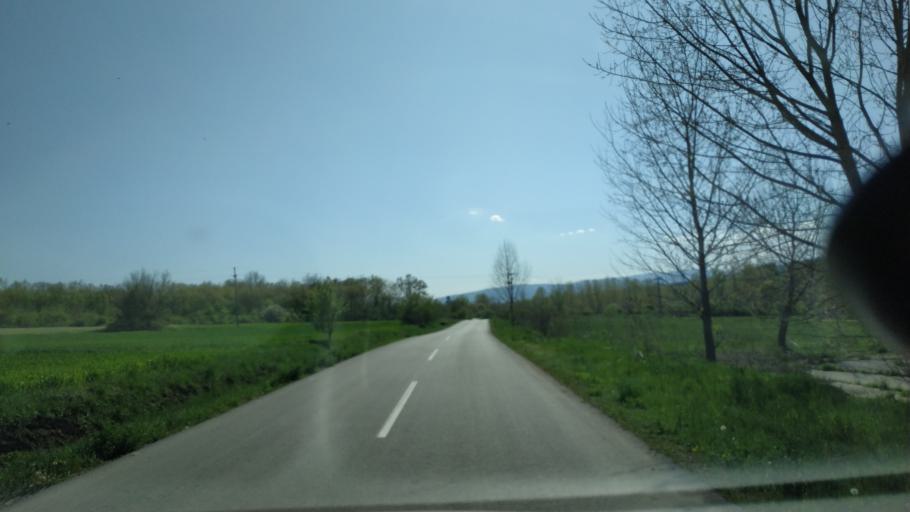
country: RS
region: Central Serbia
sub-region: Nisavski Okrug
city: Nis
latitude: 43.4603
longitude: 21.8579
